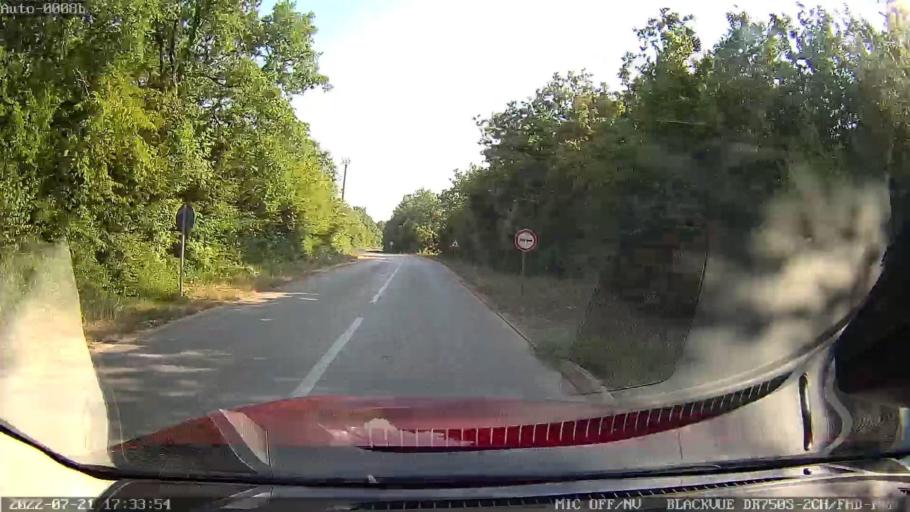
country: HR
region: Istarska
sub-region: Grad Rovinj
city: Rovinj
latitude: 45.1687
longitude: 13.7450
